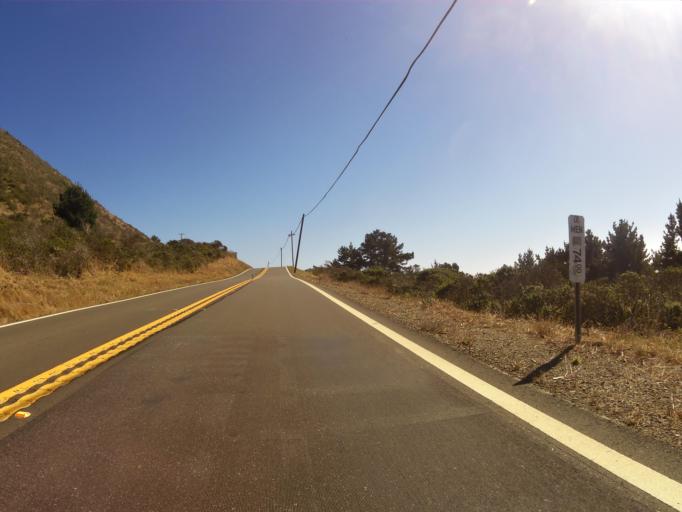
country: US
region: California
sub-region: Mendocino County
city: Fort Bragg
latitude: 39.5981
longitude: -123.7838
